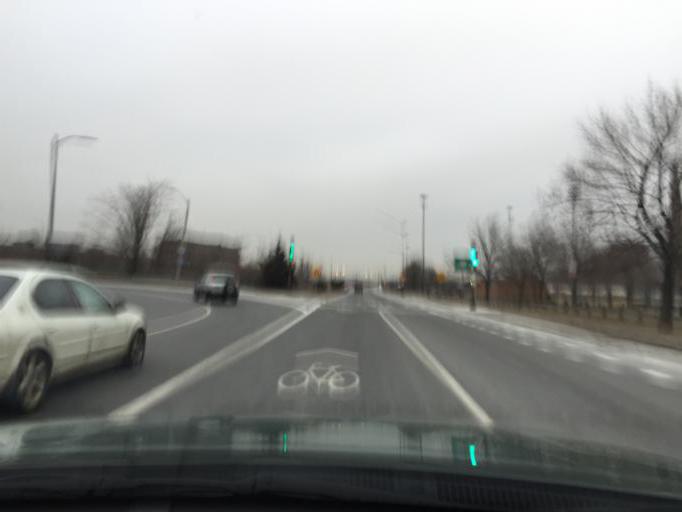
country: US
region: Massachusetts
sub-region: Middlesex County
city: Somerville
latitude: 42.3847
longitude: -71.0727
